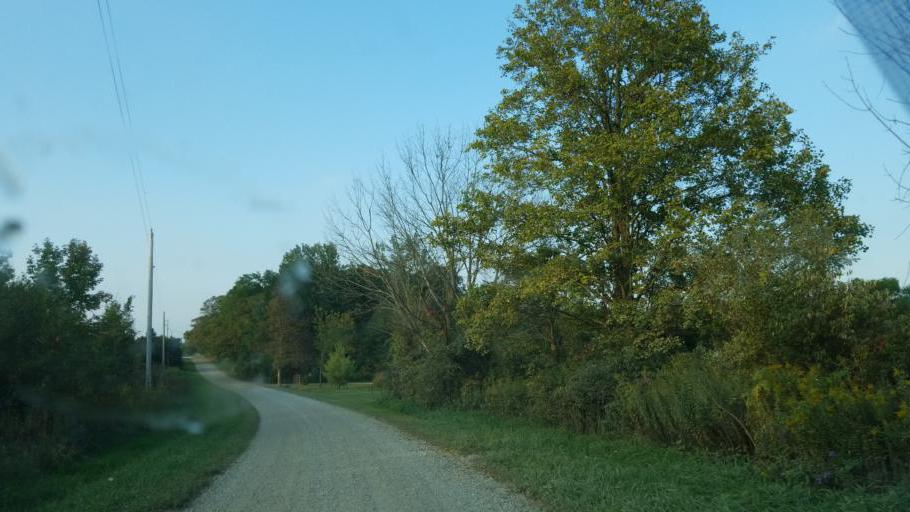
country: US
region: Ohio
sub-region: Knox County
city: Fredericktown
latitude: 40.4365
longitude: -82.6447
